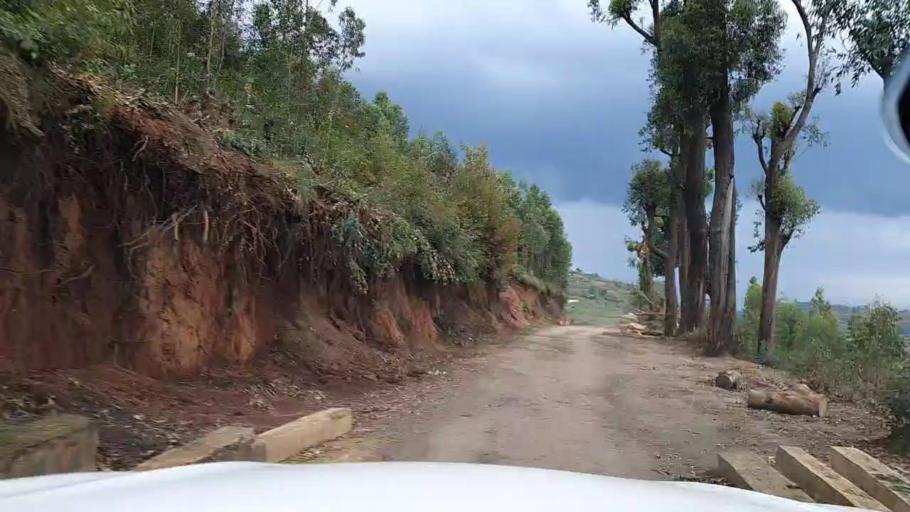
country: BI
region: Kayanza
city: Kayanza
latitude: -2.7929
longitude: 29.5171
